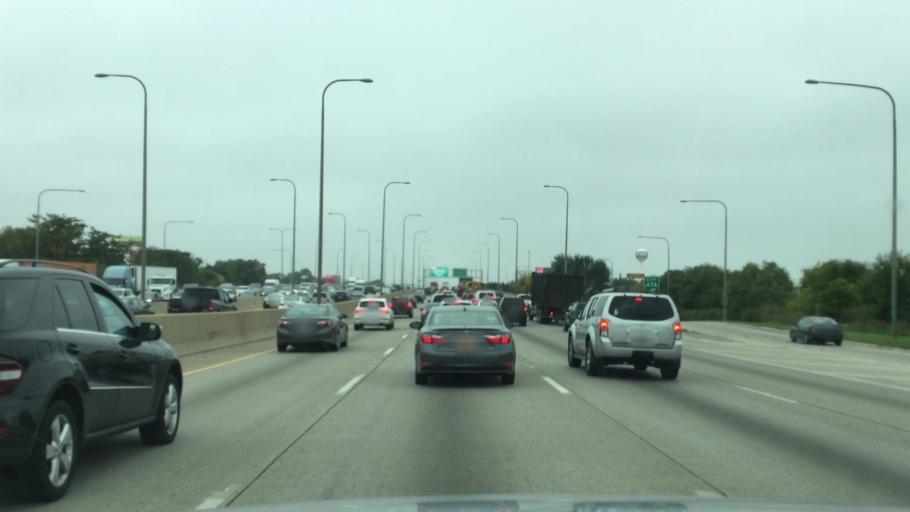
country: US
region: Illinois
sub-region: Cook County
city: Chicago
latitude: 41.9237
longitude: -87.6821
